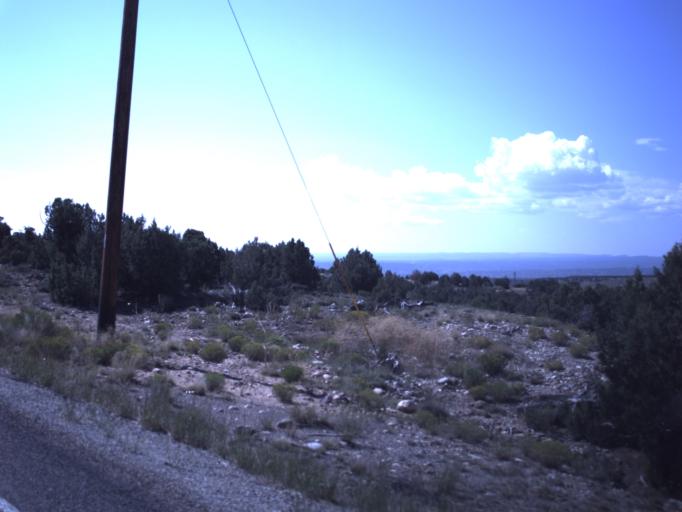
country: US
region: Utah
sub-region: Duchesne County
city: Duchesne
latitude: 40.2558
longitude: -110.4051
